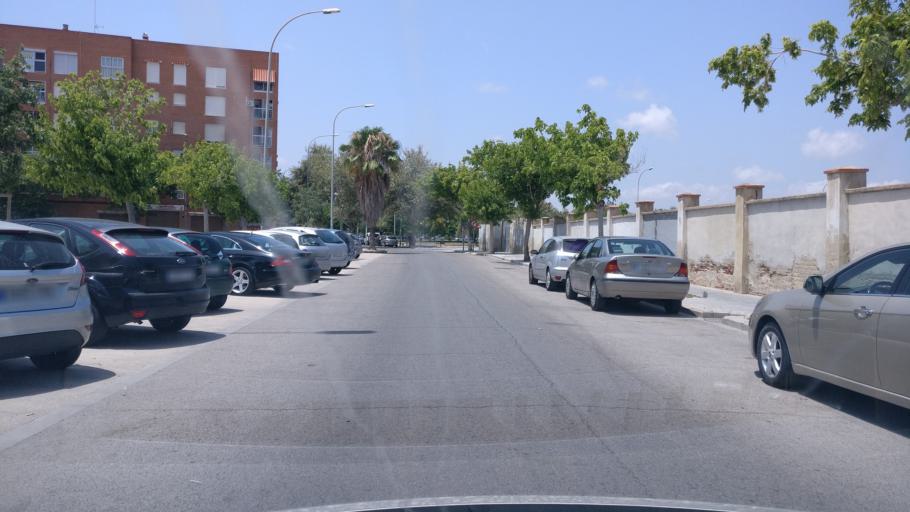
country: ES
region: Valencia
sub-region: Provincia de Valencia
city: Alboraya
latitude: 39.4802
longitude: -0.3302
